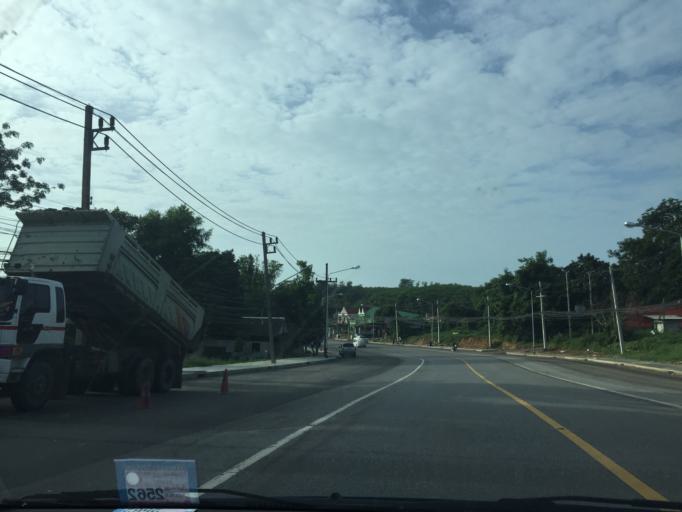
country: TH
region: Phuket
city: Mueang Phuket
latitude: 7.8355
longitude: 98.3945
